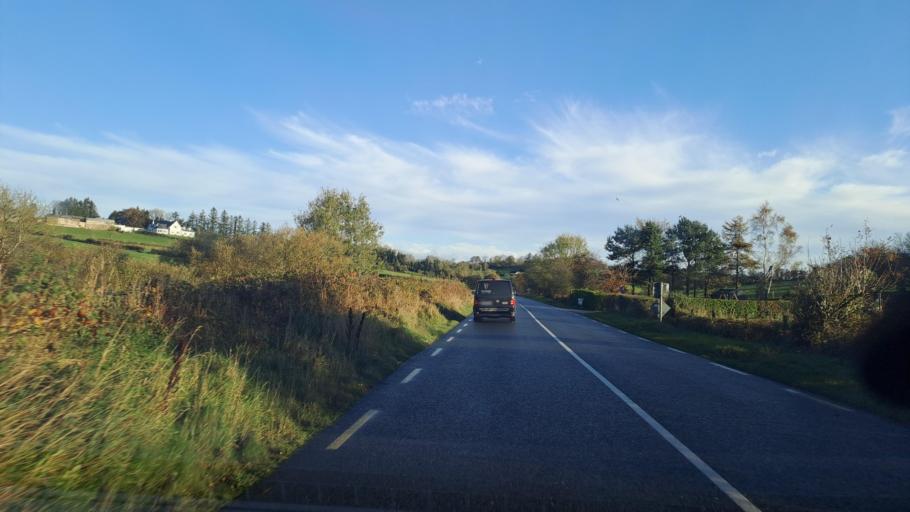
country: IE
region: Ulster
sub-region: County Monaghan
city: Monaghan
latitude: 54.1662
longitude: -7.0007
